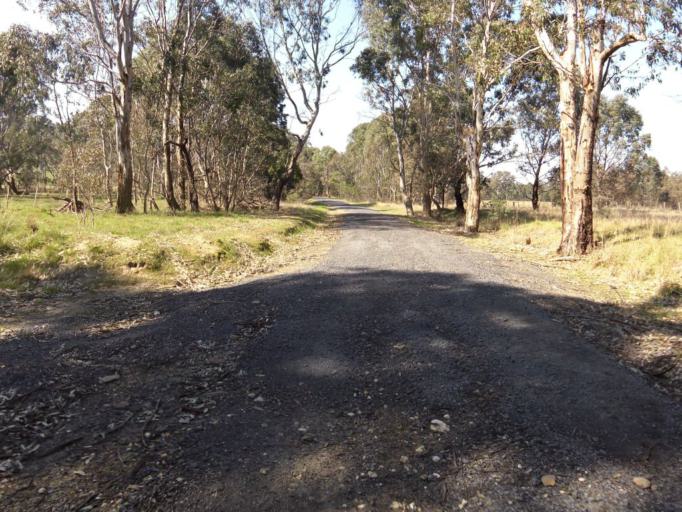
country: AU
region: Victoria
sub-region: Murrindindi
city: Alexandra
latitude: -36.9835
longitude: 145.7229
